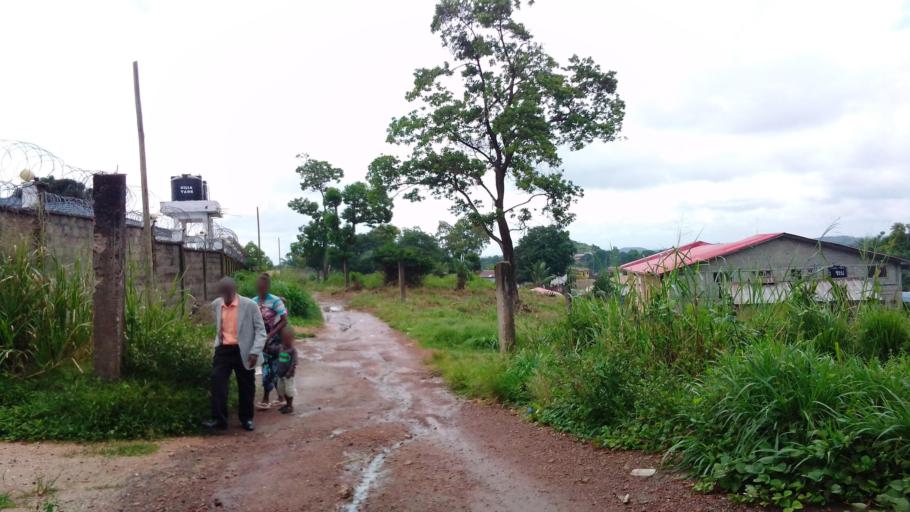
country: SL
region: Eastern Province
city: Kenema
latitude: 7.8749
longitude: -11.1751
